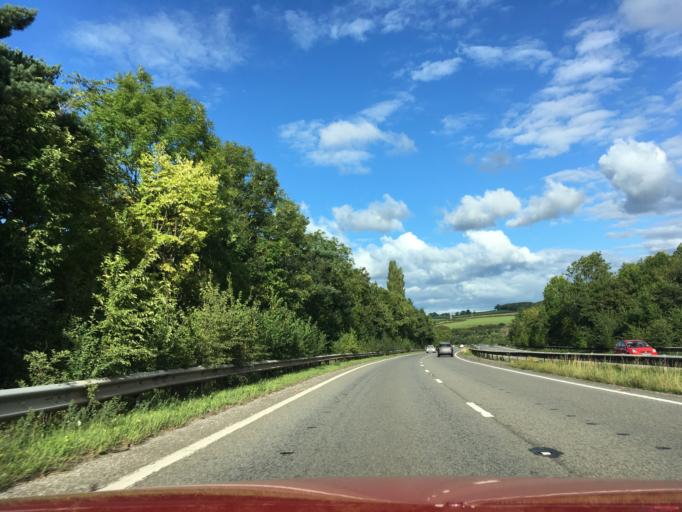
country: GB
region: England
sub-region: Devon
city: Chudleigh
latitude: 50.5829
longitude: -3.6319
